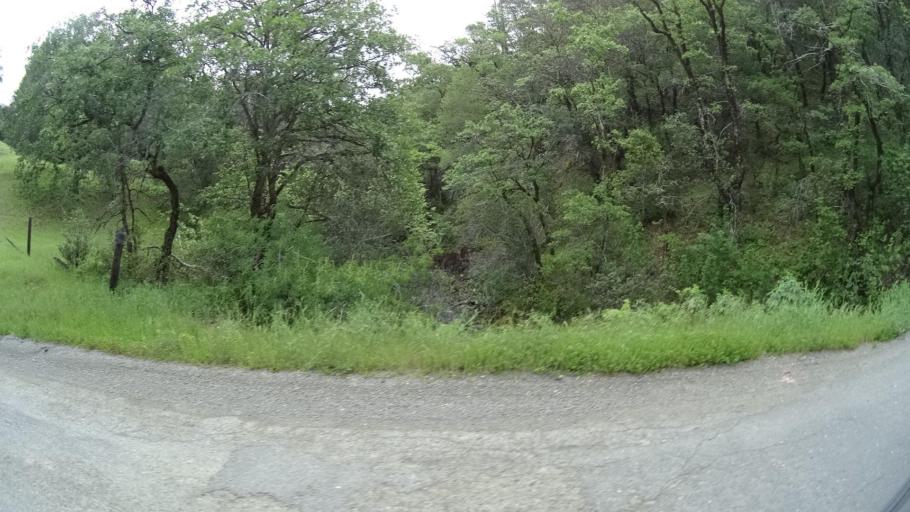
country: US
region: California
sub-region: Humboldt County
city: Redway
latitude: 40.1747
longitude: -123.5992
